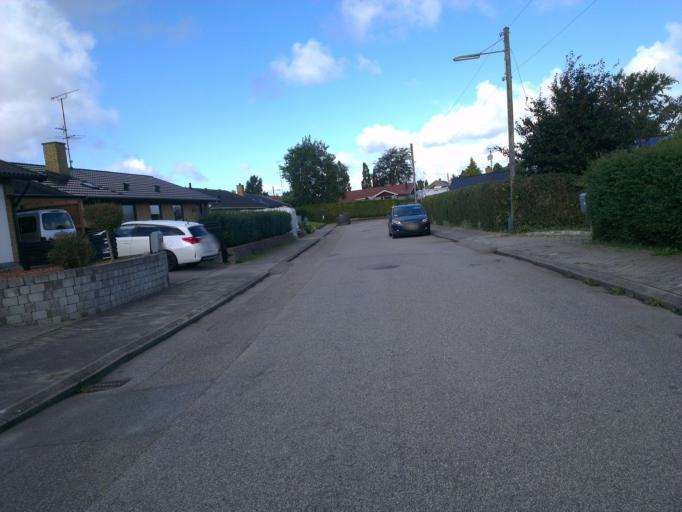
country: DK
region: Capital Region
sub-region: Frederikssund Kommune
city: Slangerup
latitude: 55.8514
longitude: 12.1712
